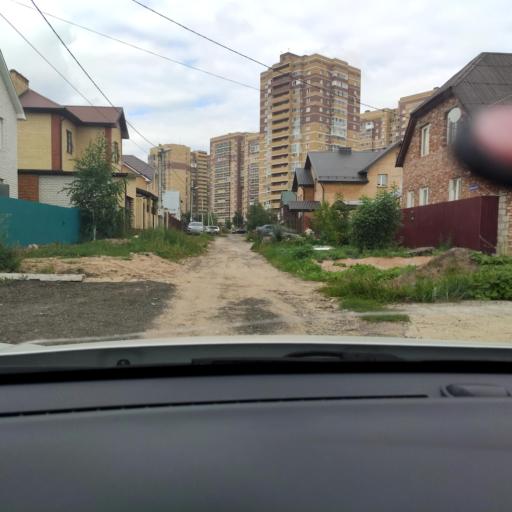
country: RU
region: Tatarstan
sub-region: Gorod Kazan'
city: Kazan
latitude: 55.7785
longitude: 49.2427
